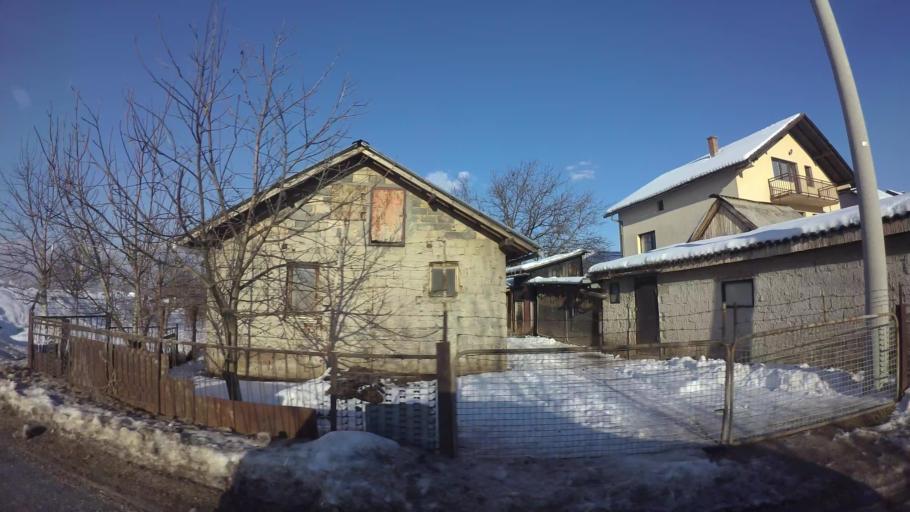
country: BA
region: Federation of Bosnia and Herzegovina
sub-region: Kanton Sarajevo
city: Sarajevo
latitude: 43.8174
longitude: 18.3428
